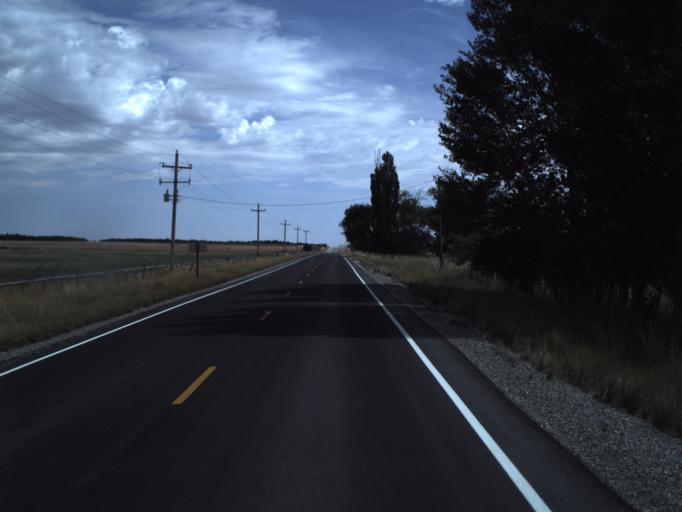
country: US
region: Idaho
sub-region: Cassia County
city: Burley
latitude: 41.8170
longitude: -113.3151
